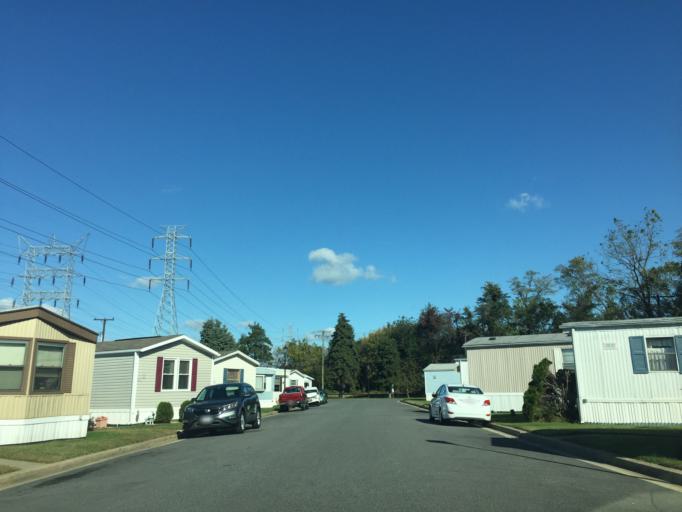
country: US
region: Maryland
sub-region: Baltimore County
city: Dundalk
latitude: 39.2548
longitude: -76.5017
